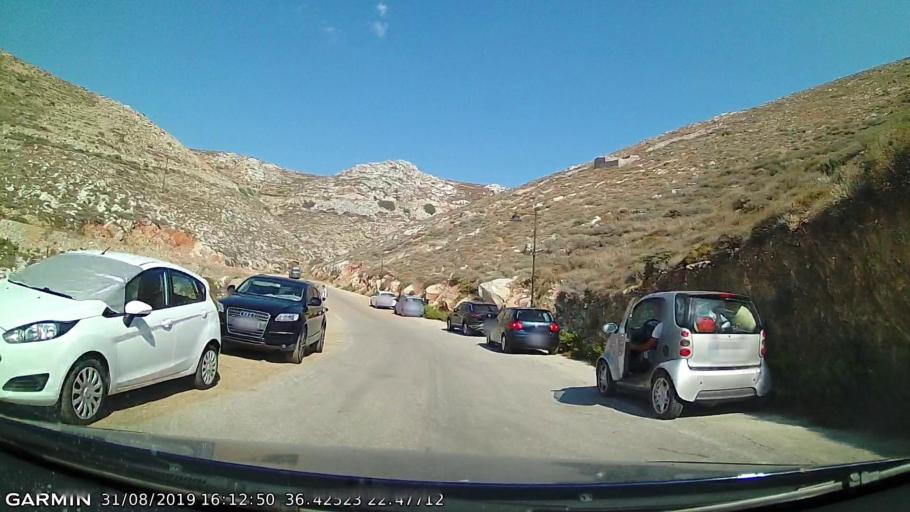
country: GR
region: Peloponnese
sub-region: Nomos Lakonias
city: Gytheio
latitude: 36.4252
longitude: 22.4771
